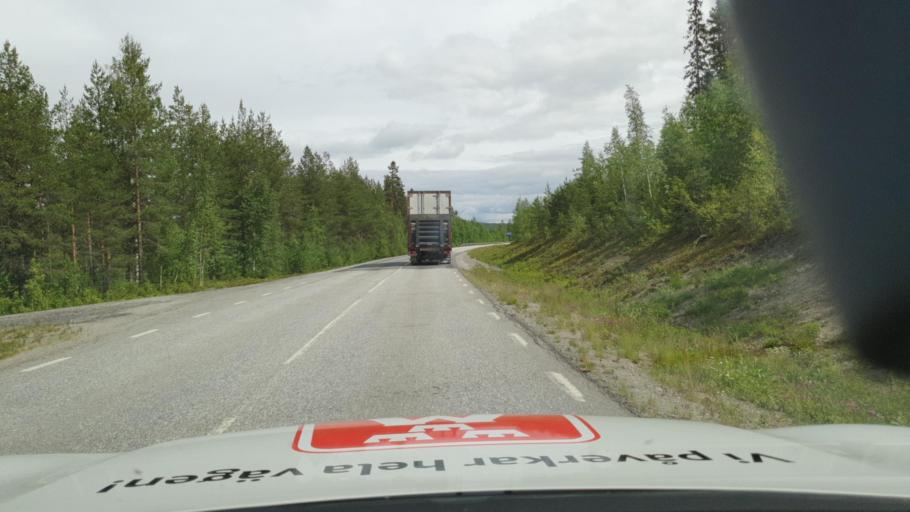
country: SE
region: Vaesterbotten
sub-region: Dorotea Kommun
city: Dorotea
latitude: 64.2384
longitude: 16.7846
